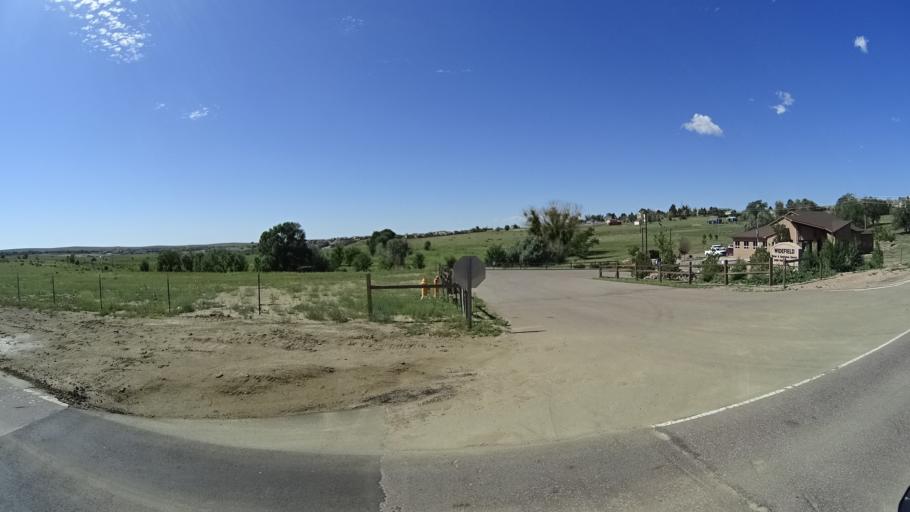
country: US
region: Colorado
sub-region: El Paso County
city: Security-Widefield
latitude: 38.7376
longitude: -104.6725
